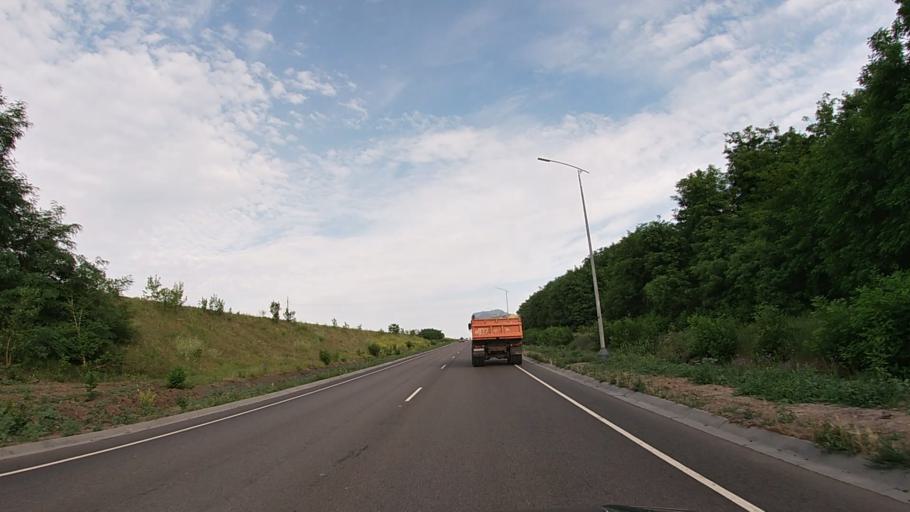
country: RU
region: Belgorod
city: Severnyy
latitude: 50.6694
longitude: 36.4875
